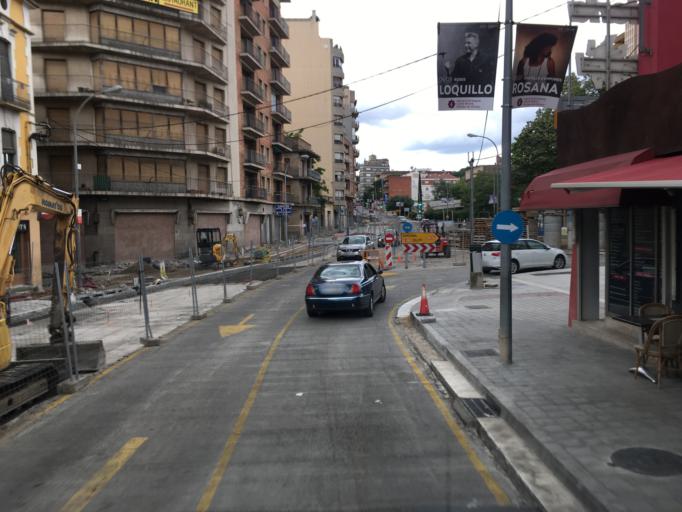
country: ES
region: Catalonia
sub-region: Provincia de Girona
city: Figueres
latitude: 42.2661
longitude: 2.9581
